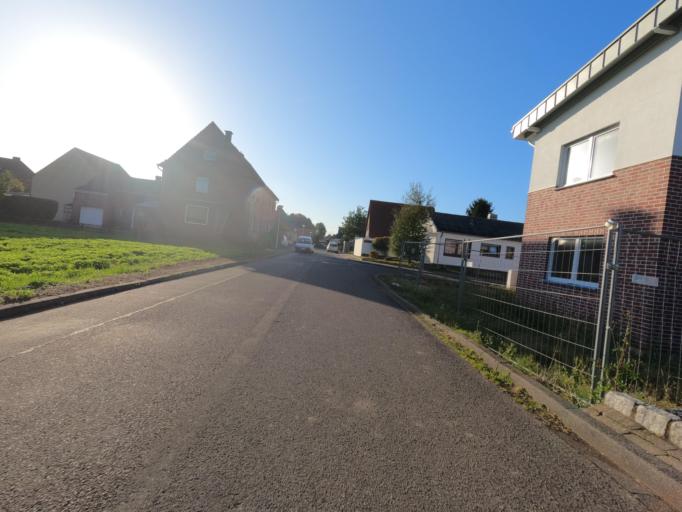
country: DE
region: North Rhine-Westphalia
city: Huckelhoven
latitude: 51.0365
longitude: 6.1751
